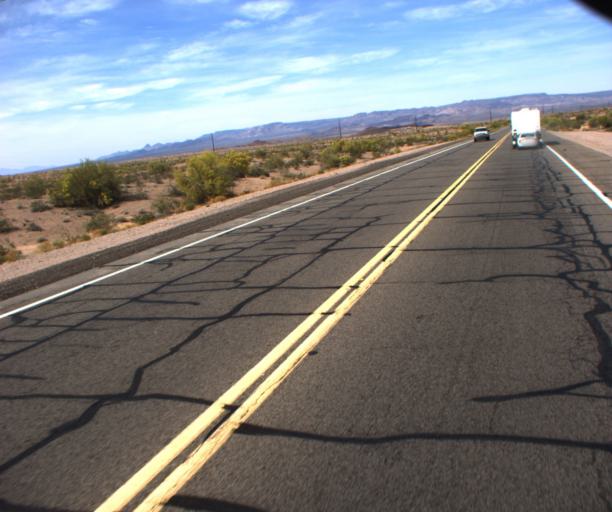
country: US
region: Arizona
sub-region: Mohave County
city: Desert Hills
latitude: 34.6500
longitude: -114.3201
